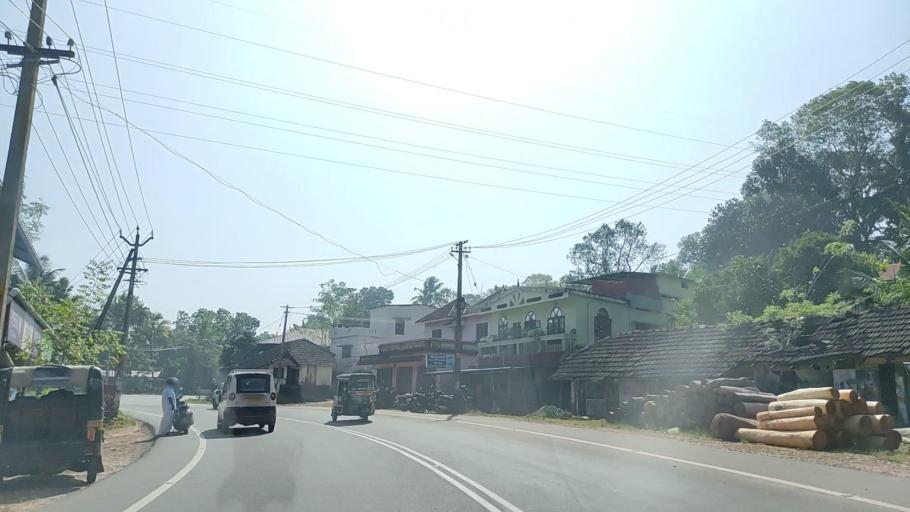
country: IN
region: Kerala
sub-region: Kollam
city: Punalur
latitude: 8.9332
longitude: 76.9624
